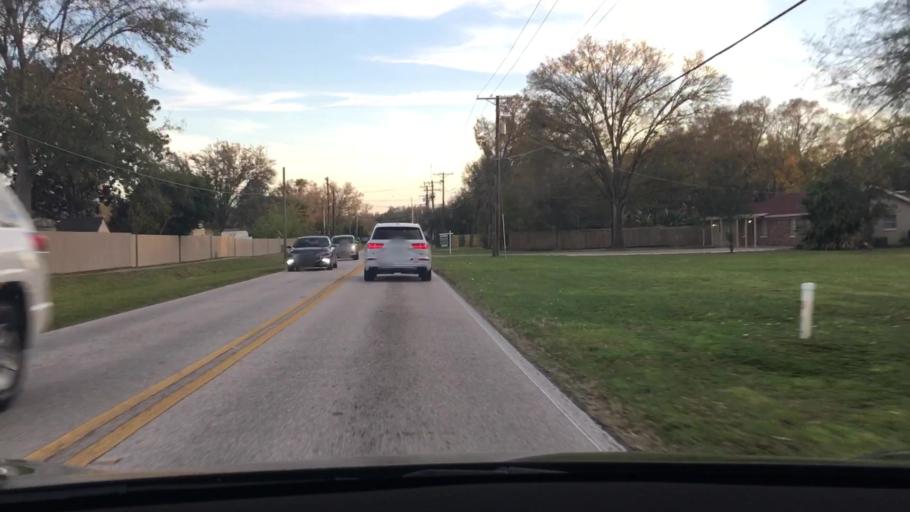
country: US
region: Florida
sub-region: Hillsborough County
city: Greater Northdale
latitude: 28.0883
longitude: -82.5399
